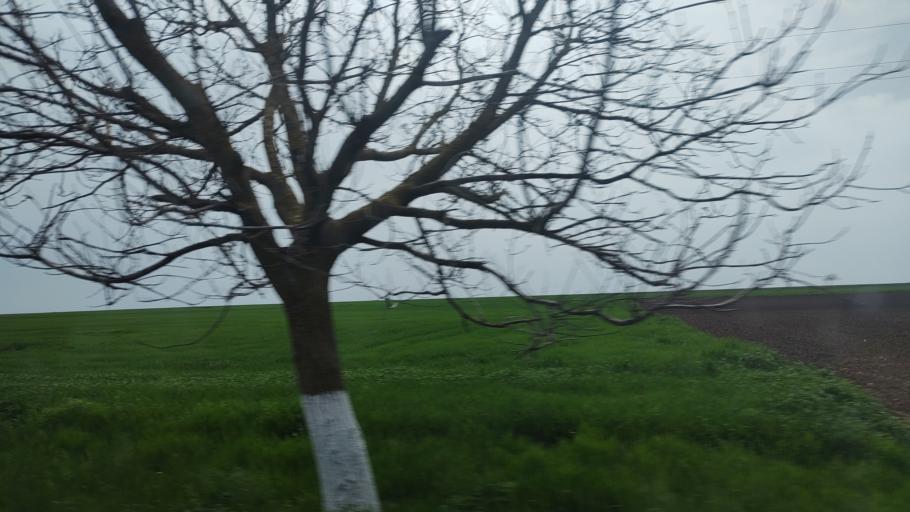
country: RO
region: Constanta
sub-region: Comuna Ciocarlia
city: Ciocarlia de Sus
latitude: 44.1109
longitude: 28.3097
